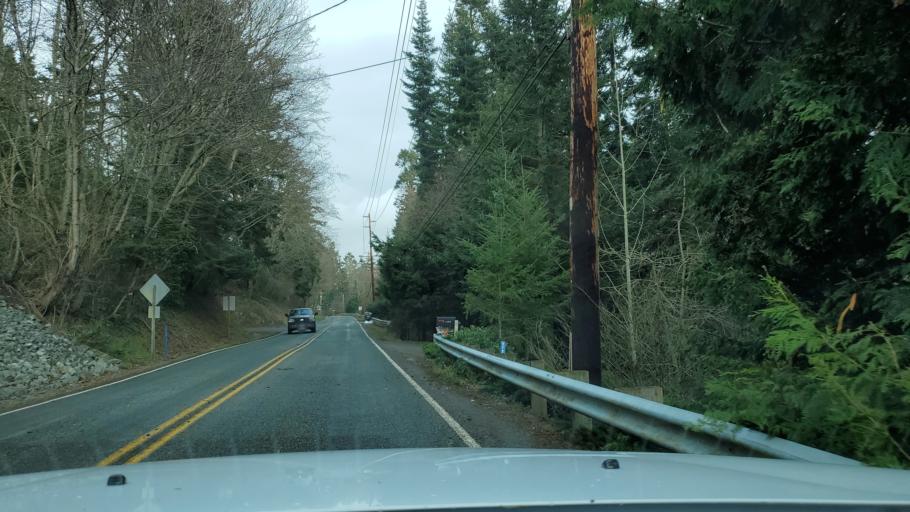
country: US
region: Washington
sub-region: Skagit County
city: Anacortes
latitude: 48.4246
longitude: -122.5953
